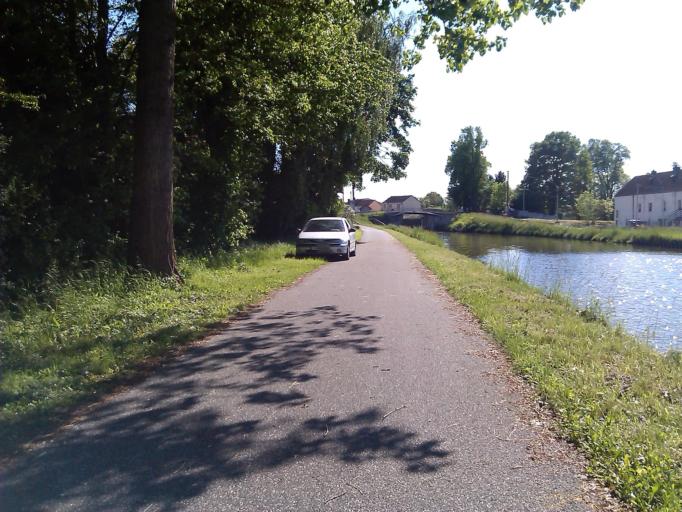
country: FR
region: Bourgogne
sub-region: Departement de Saone-et-Loire
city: Ecuisses
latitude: 46.7631
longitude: 4.5227
